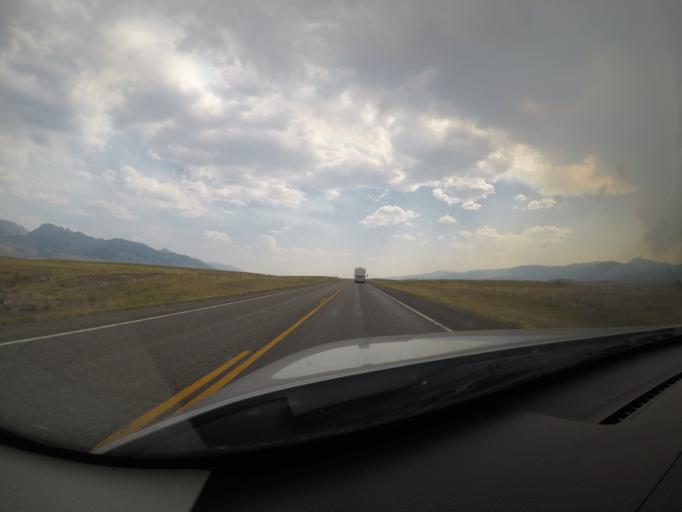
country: US
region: Montana
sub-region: Gallatin County
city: Big Sky
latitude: 45.0901
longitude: -111.6479
